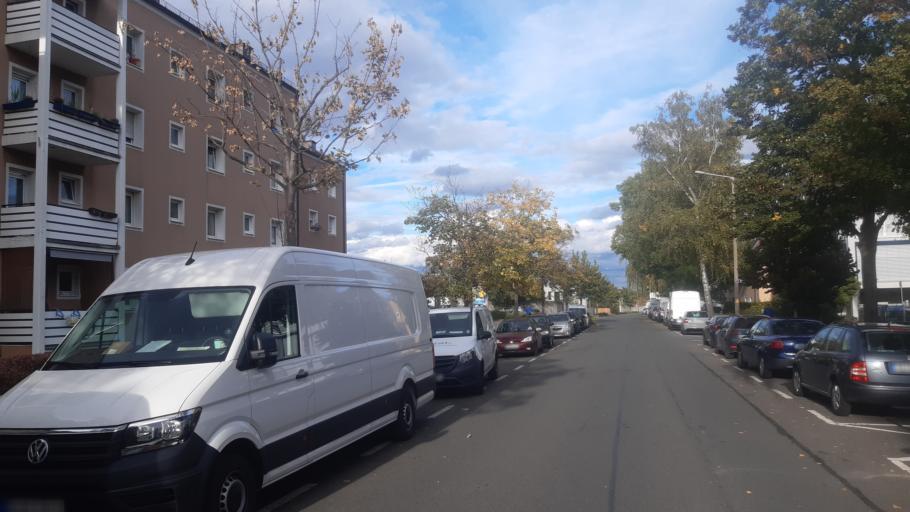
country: DE
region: Bavaria
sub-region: Regierungsbezirk Mittelfranken
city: Nuernberg
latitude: 49.4271
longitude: 11.0940
